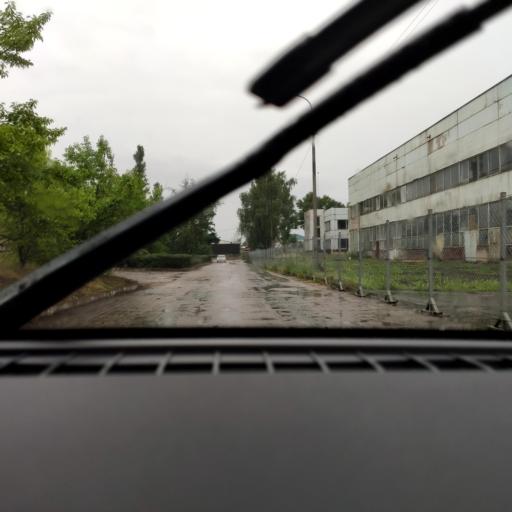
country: RU
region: Voronezj
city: Somovo
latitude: 51.7153
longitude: 39.2883
